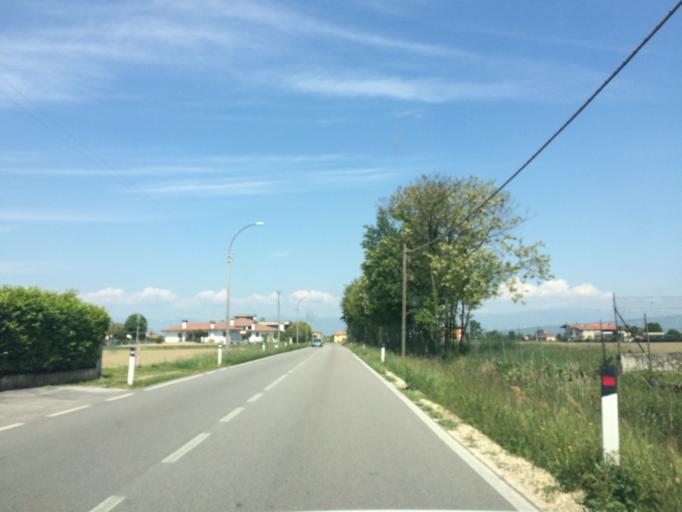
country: IT
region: Veneto
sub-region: Provincia di Padova
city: Fontaniva
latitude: 45.6129
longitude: 11.7707
